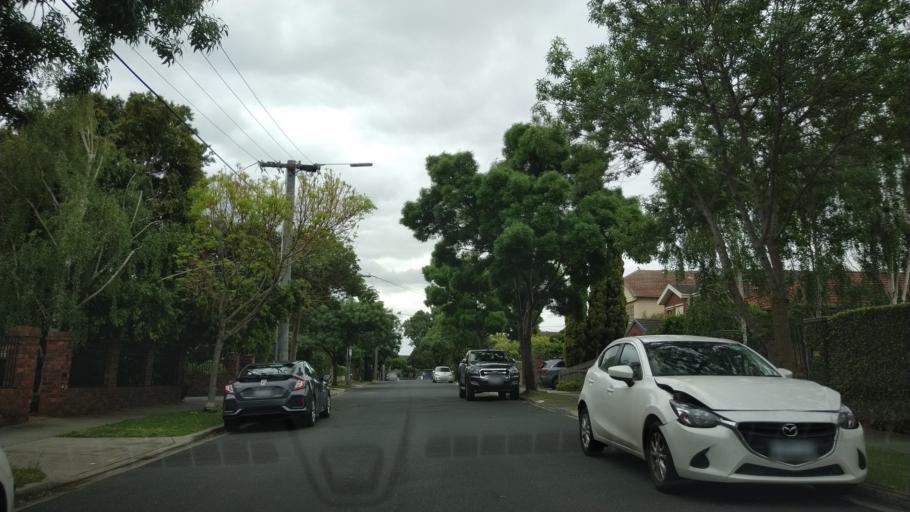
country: AU
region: Victoria
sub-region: Glen Eira
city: Caulfield South
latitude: -37.8874
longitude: 145.0323
